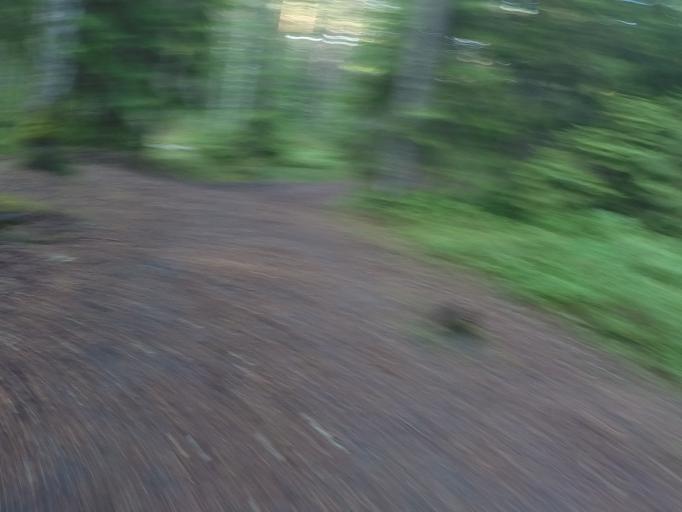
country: SE
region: Soedermanland
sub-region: Eskilstuna Kommun
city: Hallbybrunn
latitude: 59.3955
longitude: 16.4055
